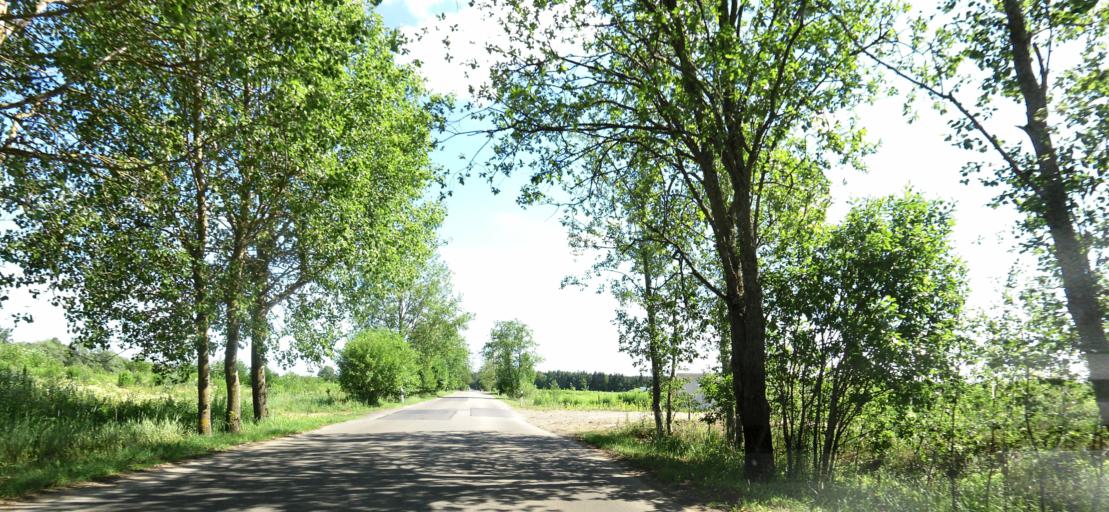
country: LT
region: Vilnius County
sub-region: Vilnius
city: Fabijoniskes
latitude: 54.8097
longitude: 25.3248
